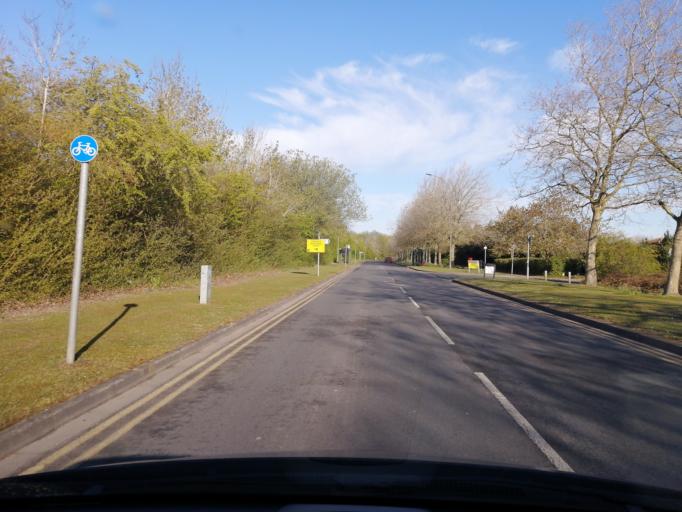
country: GB
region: England
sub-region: Peterborough
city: Castor
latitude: 52.5549
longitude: -0.3139
